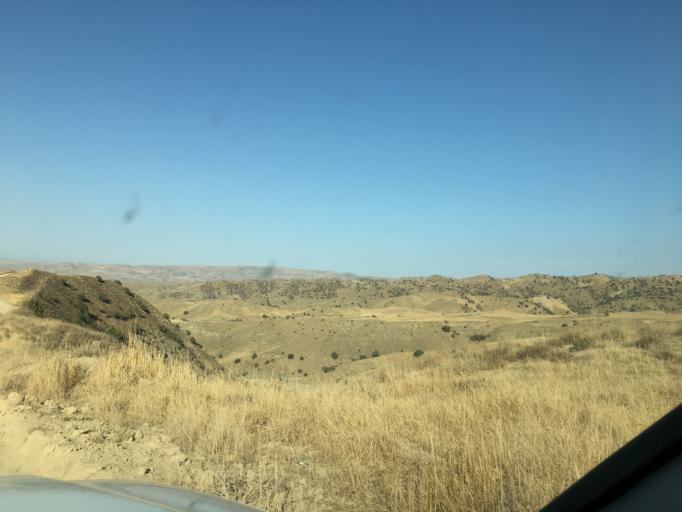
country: TM
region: Balkan
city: Magtymguly
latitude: 38.3065
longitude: 56.8318
